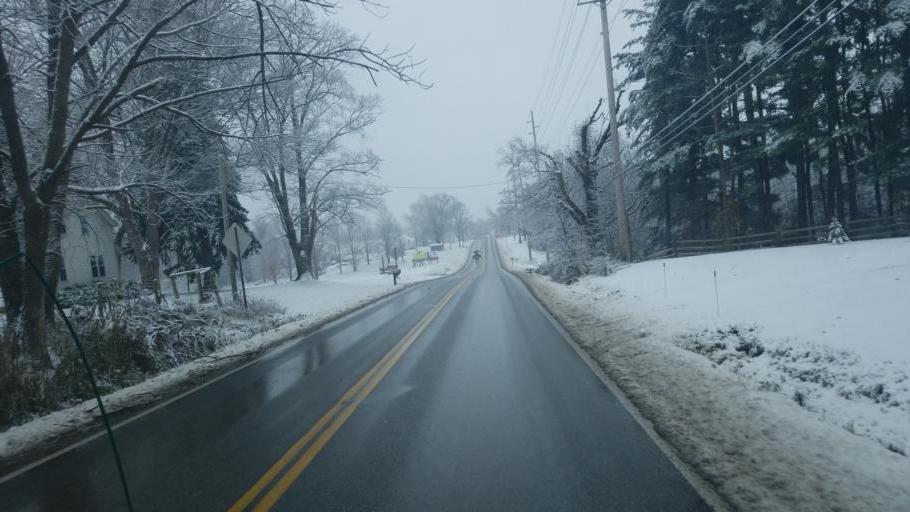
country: US
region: Ohio
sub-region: Geauga County
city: Middlefield
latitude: 41.4423
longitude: -81.0646
